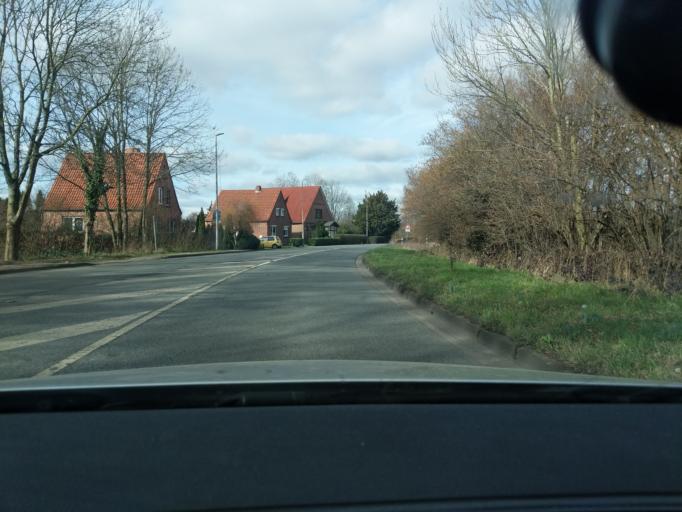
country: DE
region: Lower Saxony
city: Stade
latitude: 53.6563
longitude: 9.4766
